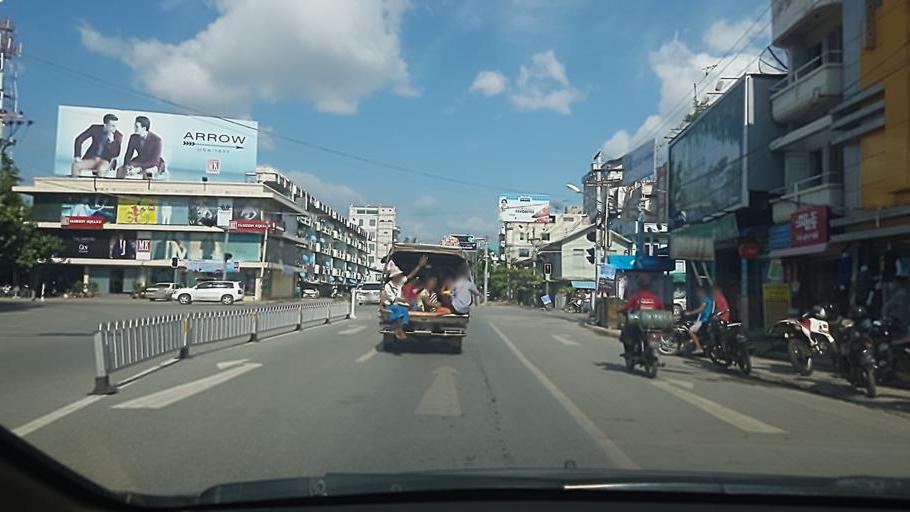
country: MM
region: Mandalay
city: Mandalay
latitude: 21.9693
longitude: 96.0832
